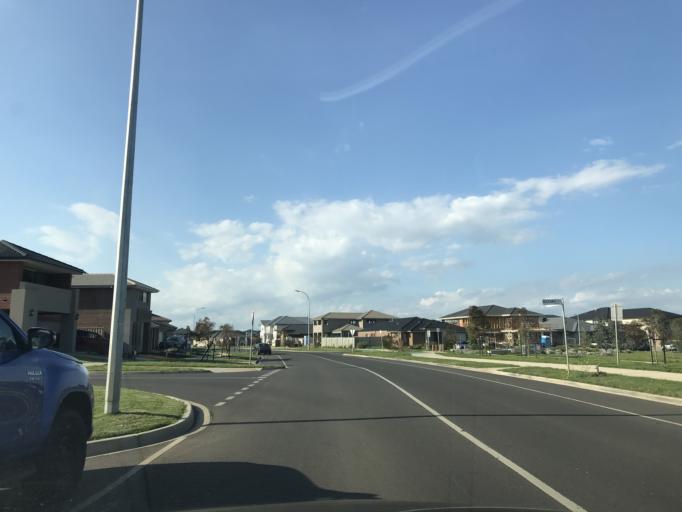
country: AU
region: Victoria
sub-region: Wyndham
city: Hoppers Crossing
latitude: -37.8875
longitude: 144.7142
